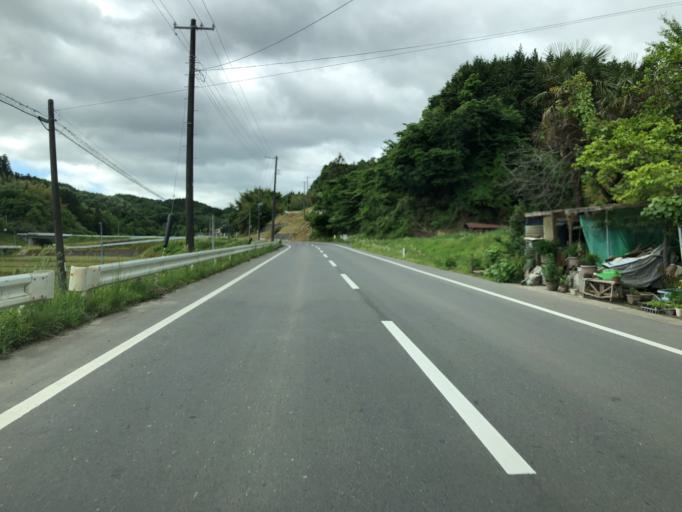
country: JP
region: Fukushima
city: Nihommatsu
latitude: 37.5459
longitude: 140.4602
